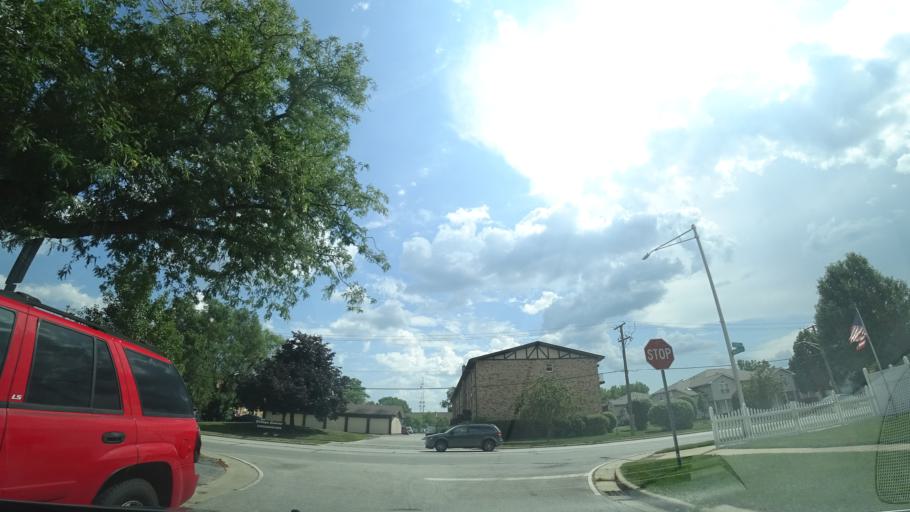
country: US
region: Illinois
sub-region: Cook County
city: Merrionette Park
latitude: 41.6696
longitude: -87.7158
